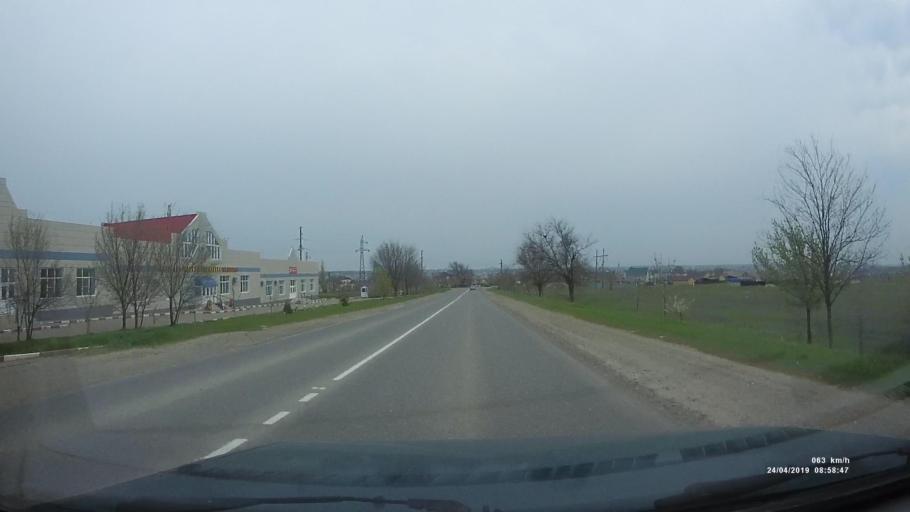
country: RU
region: Kalmykiya
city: Arshan'
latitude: 46.3104
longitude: 44.2017
